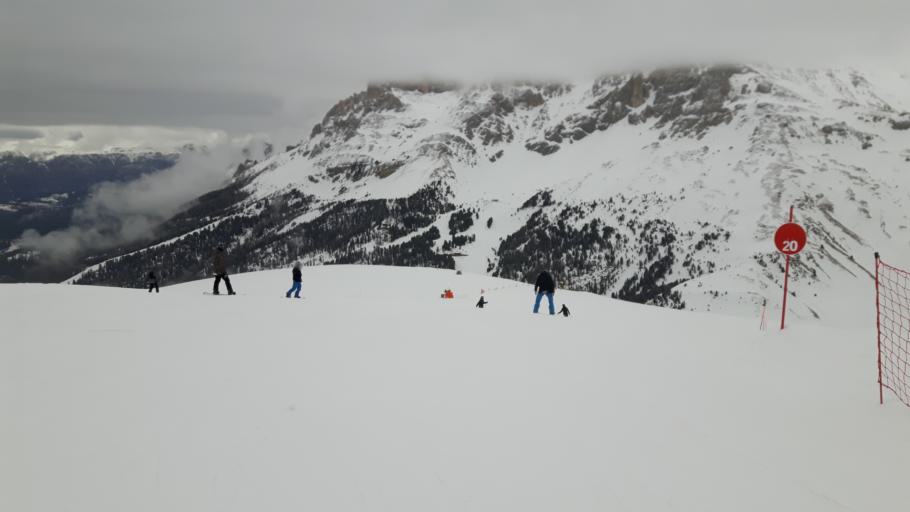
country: IT
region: Trentino-Alto Adige
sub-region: Provincia di Trento
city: Tesero
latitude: 46.3475
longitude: 11.5273
